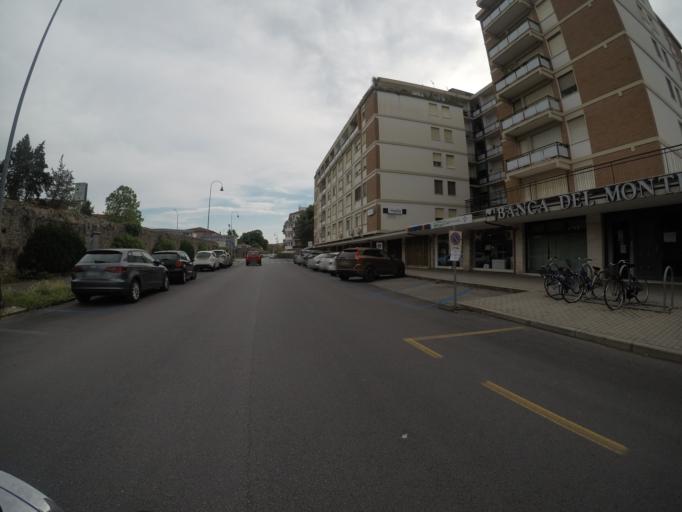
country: IT
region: Tuscany
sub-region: Province of Pisa
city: Pisa
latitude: 43.7195
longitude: 10.4111
